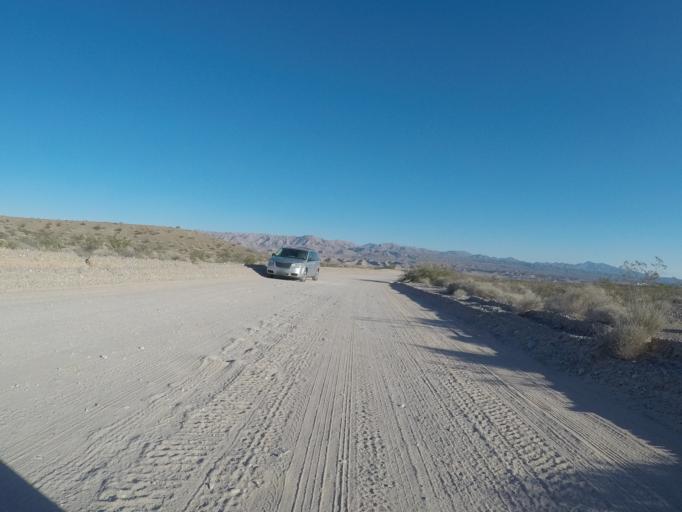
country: US
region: Nevada
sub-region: Clark County
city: Moapa Valley
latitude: 36.3871
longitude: -114.4146
